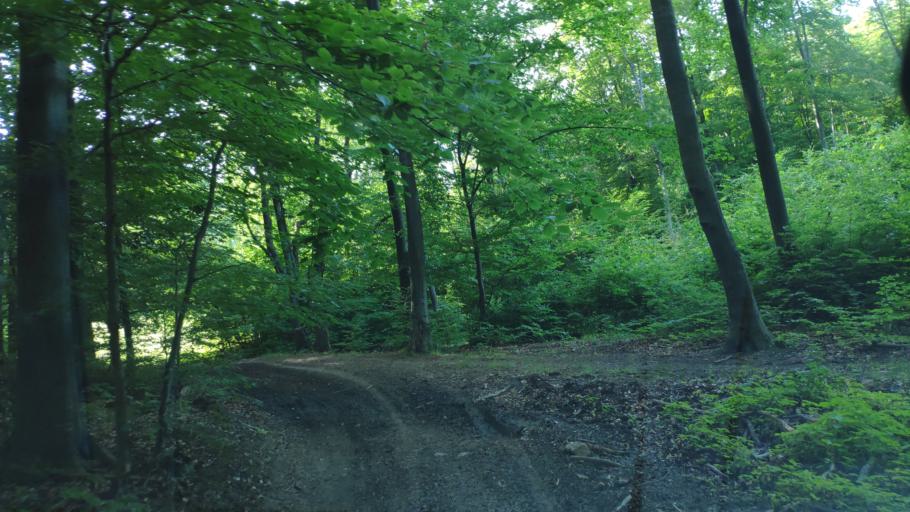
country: SK
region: Presovsky
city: Vranov nad Topl'ou
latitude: 48.8150
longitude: 21.5923
